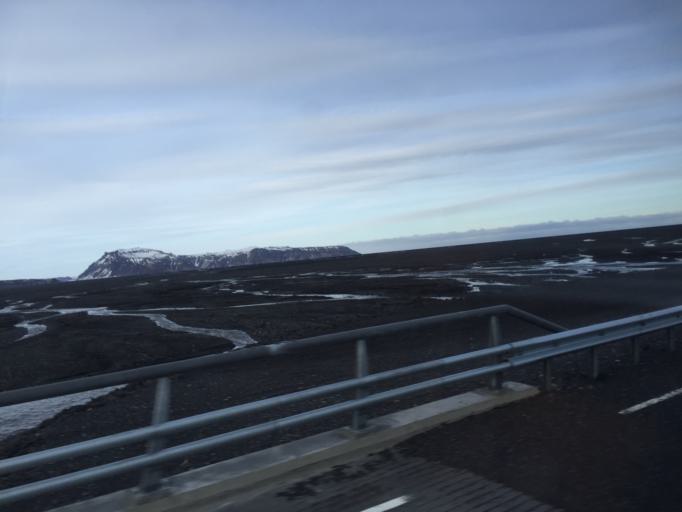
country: IS
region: South
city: Vestmannaeyjar
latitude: 63.4377
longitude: -18.8467
